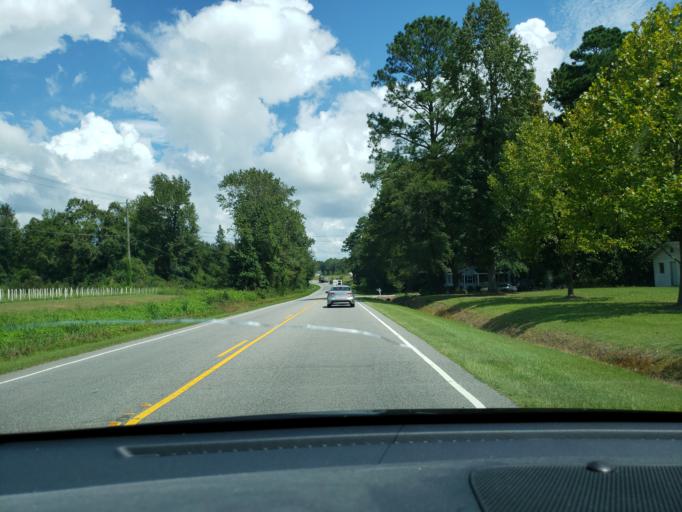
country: US
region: North Carolina
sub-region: Columbus County
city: Brunswick
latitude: 34.2589
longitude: -78.7457
